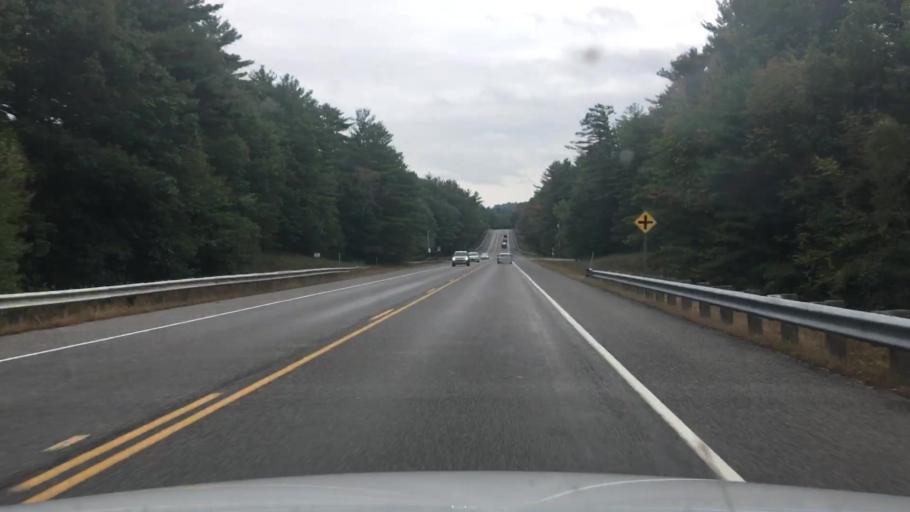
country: US
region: New Hampshire
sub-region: Carroll County
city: Wolfeboro
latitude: 43.4990
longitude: -71.2608
